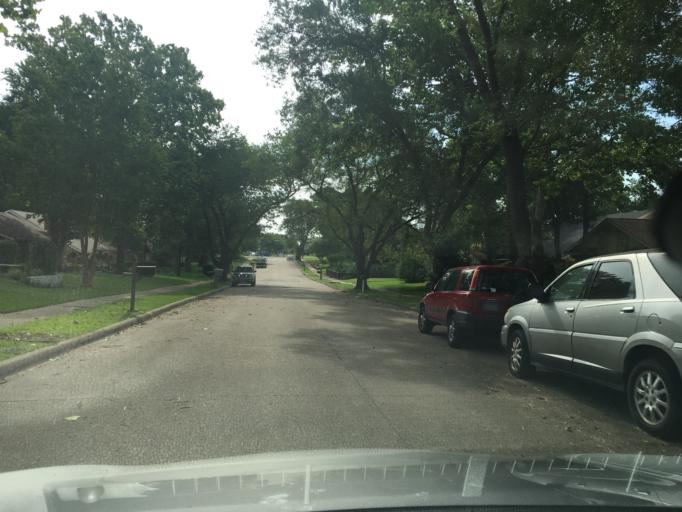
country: US
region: Texas
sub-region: Collin County
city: Plano
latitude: 32.9665
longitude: -96.6720
